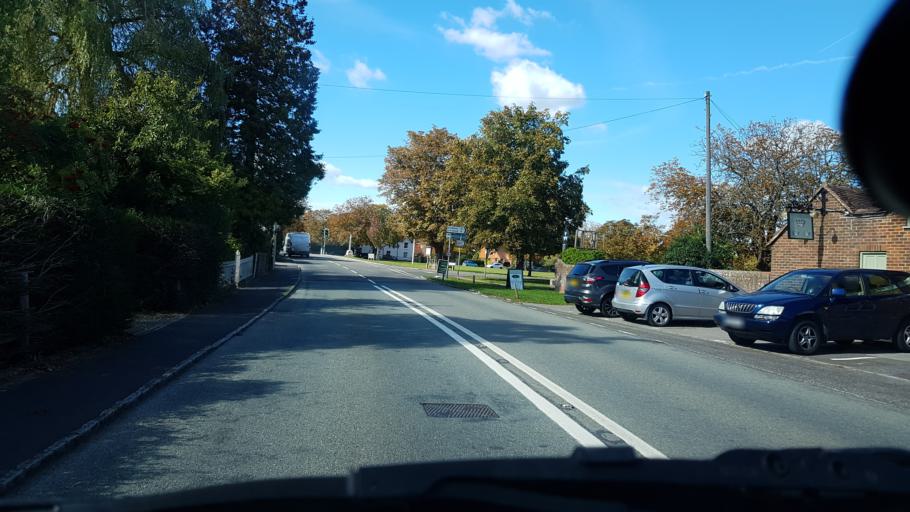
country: GB
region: England
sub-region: West Sussex
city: Billingshurst
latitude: 51.0228
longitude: -0.5038
